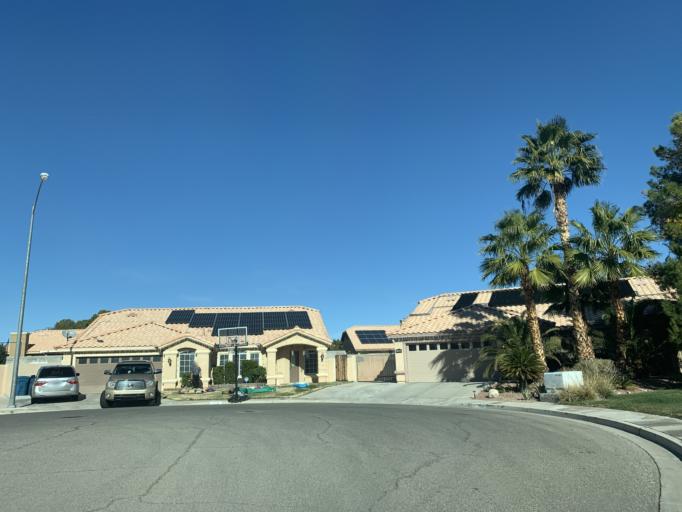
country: US
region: Nevada
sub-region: Clark County
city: Summerlin South
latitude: 36.1178
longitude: -115.2894
